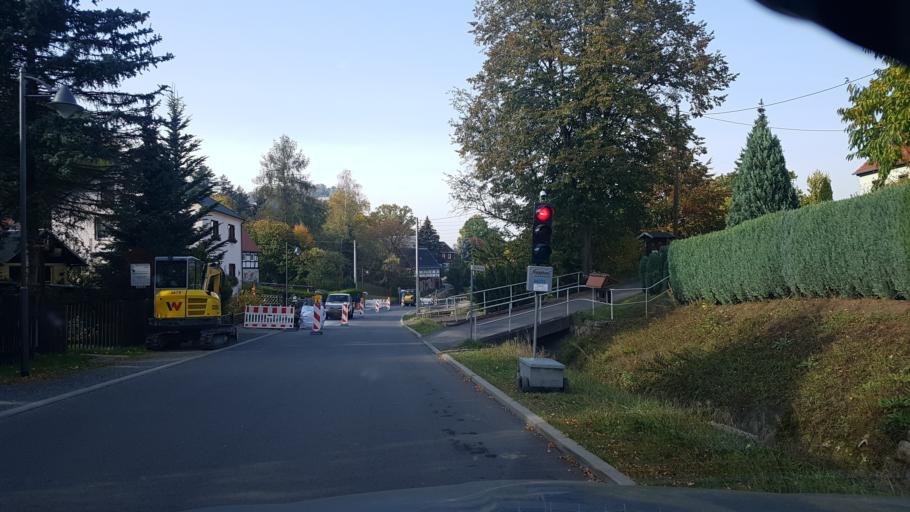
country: DE
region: Saxony
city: Konigstein
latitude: 50.9105
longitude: 14.0758
